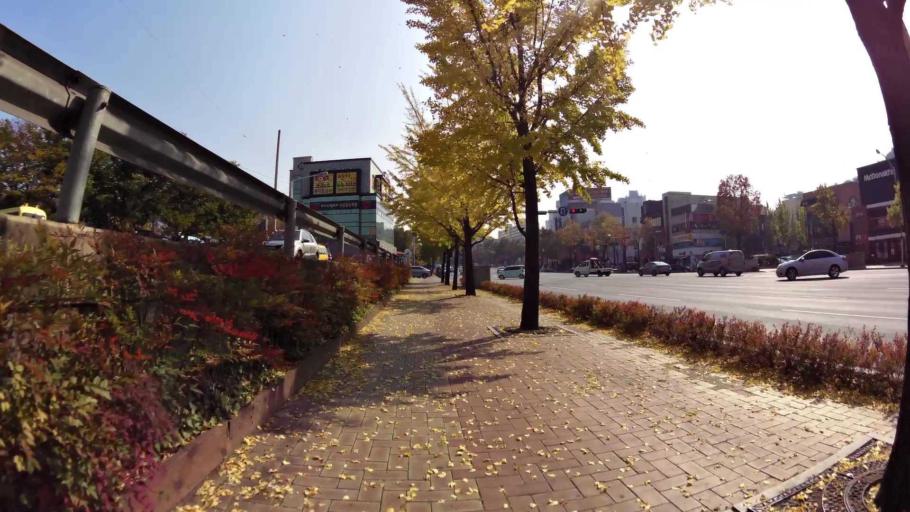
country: KR
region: Daegu
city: Daegu
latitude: 35.8571
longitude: 128.6500
